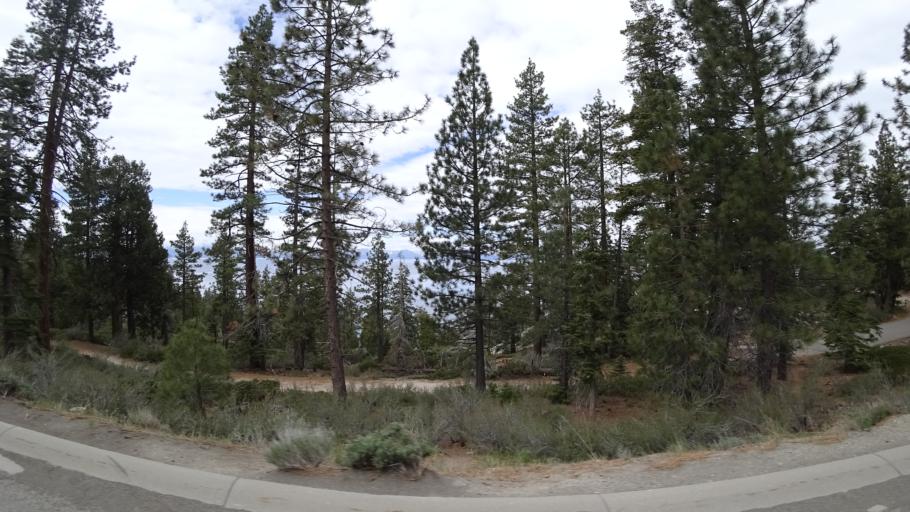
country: US
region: Nevada
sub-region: Washoe County
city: Incline Village
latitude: 39.1630
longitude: -119.9303
